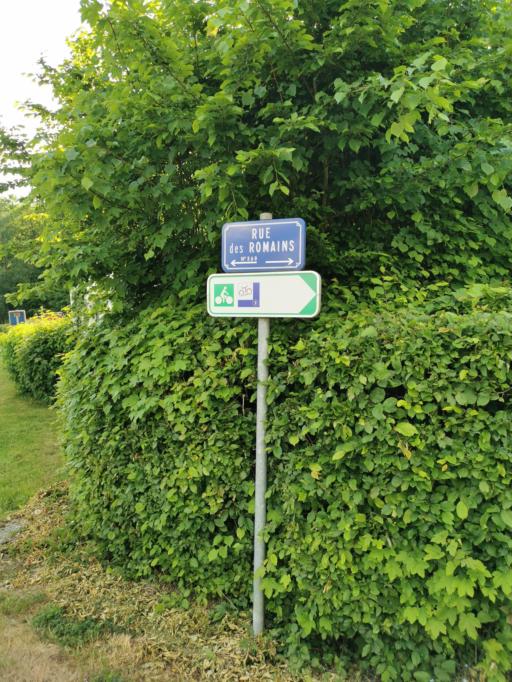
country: FR
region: Nord-Pas-de-Calais
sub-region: Departement du Nord
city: Anor
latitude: 49.9834
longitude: 4.0872
